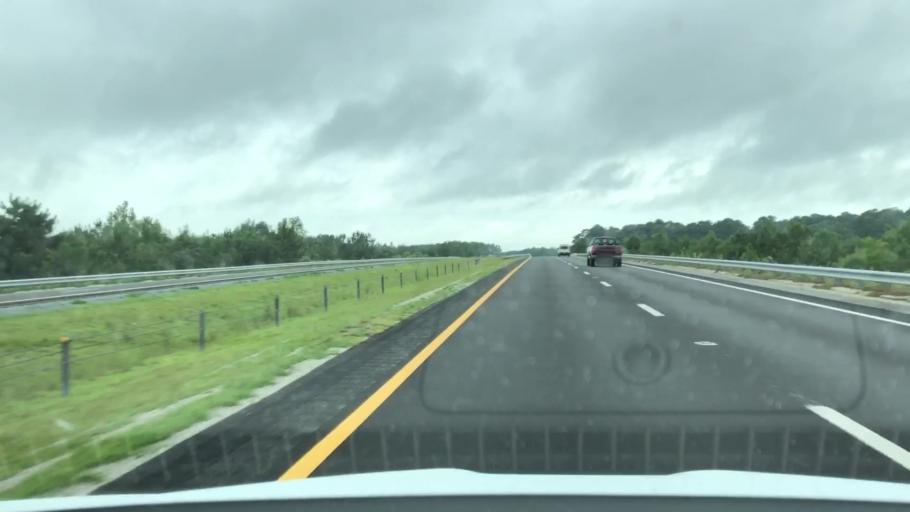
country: US
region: North Carolina
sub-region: Wayne County
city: Fremont
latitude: 35.4670
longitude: -77.9863
